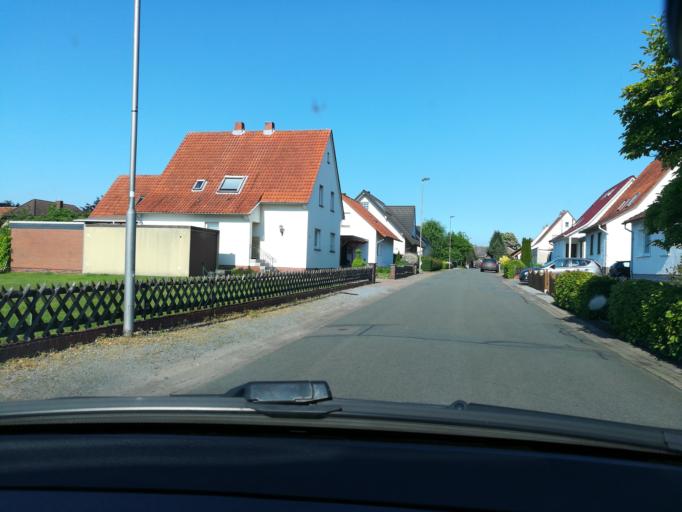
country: DE
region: North Rhine-Westphalia
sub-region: Regierungsbezirk Detmold
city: Minden
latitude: 52.3126
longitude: 8.9323
